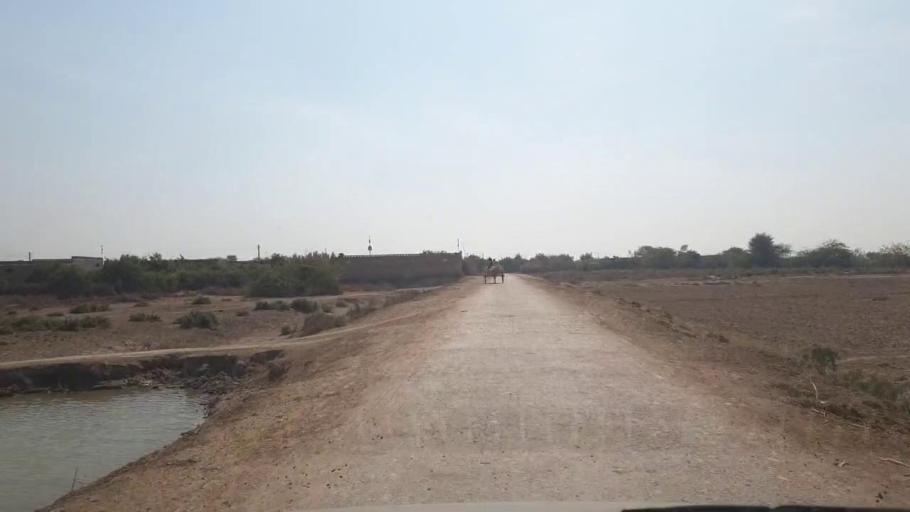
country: PK
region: Sindh
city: Chambar
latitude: 25.3403
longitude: 68.8116
